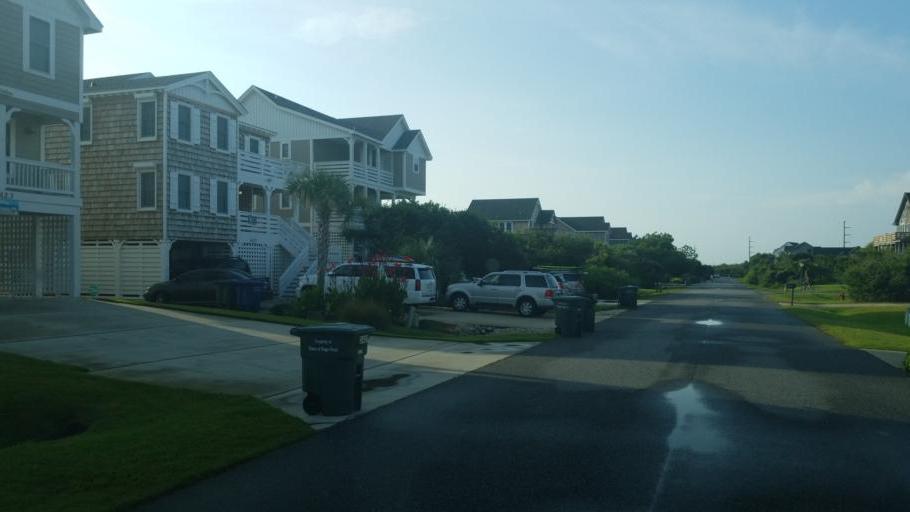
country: US
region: North Carolina
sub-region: Dare County
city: Nags Head
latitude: 35.9708
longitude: -75.6334
